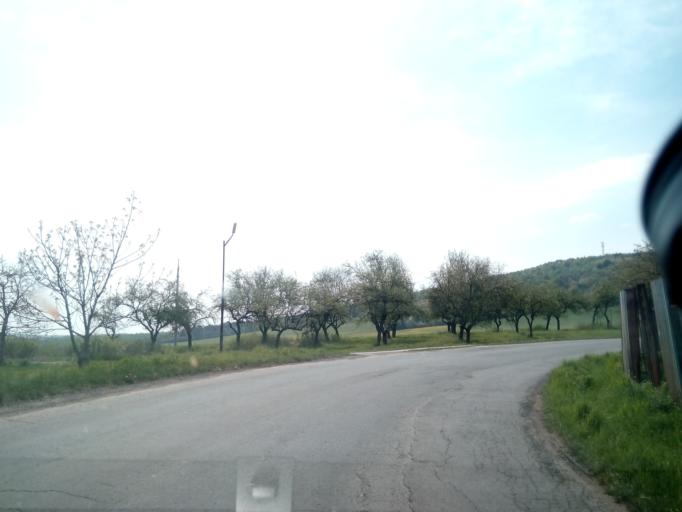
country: SK
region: Presovsky
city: Giraltovce
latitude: 49.0034
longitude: 21.5395
